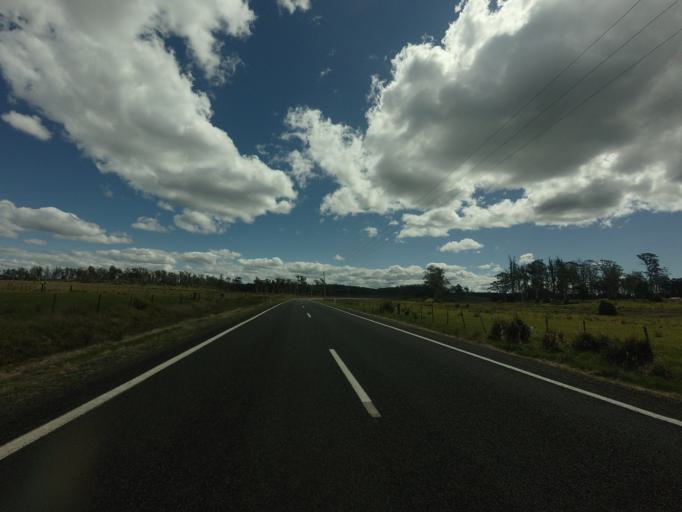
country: AU
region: Tasmania
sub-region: Northern Midlands
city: Evandale
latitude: -41.9905
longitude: 147.6836
